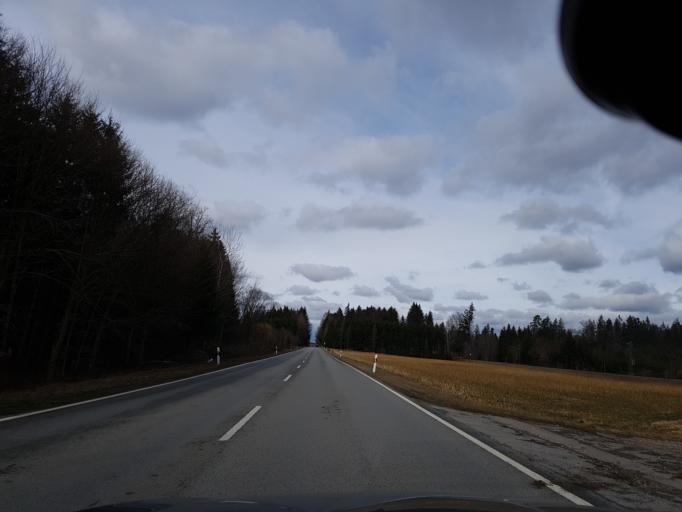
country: DE
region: Bavaria
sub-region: Upper Bavaria
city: Aying
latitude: 47.9795
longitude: 11.7543
